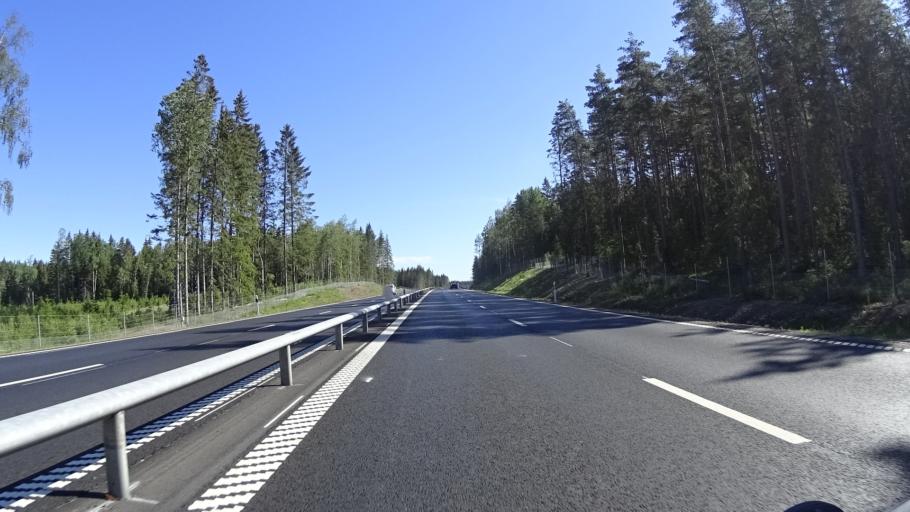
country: SE
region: Vaestra Goetaland
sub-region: Gullspangs Kommun
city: Hova
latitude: 58.8300
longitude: 14.1734
